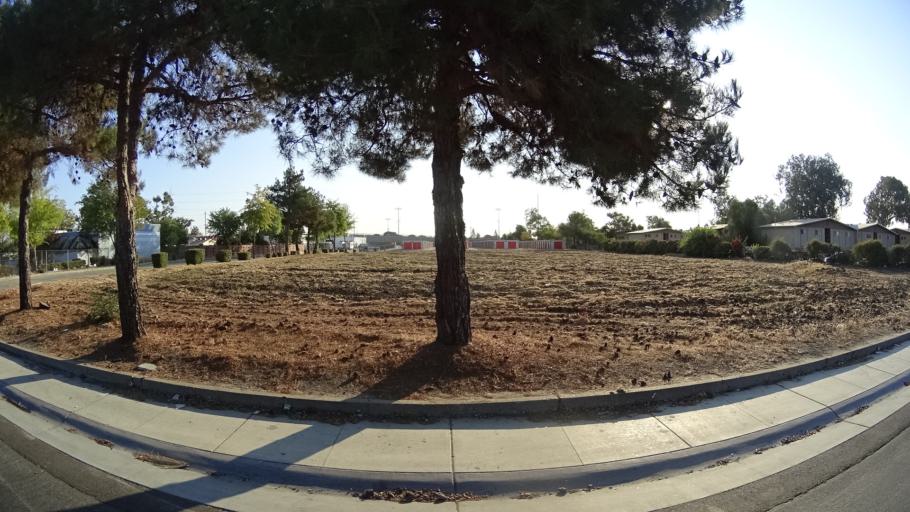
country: US
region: California
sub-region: Sacramento County
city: Parkway
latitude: 38.4947
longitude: -121.4736
